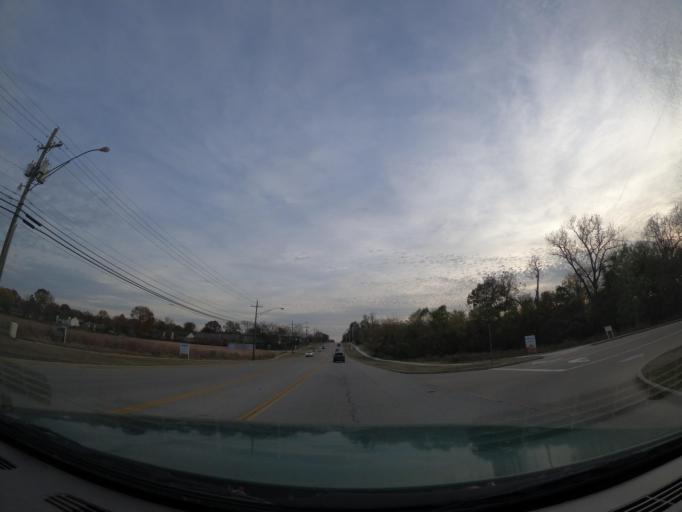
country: US
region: Oklahoma
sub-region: Tulsa County
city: Broken Arrow
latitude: 35.9875
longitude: -95.7974
